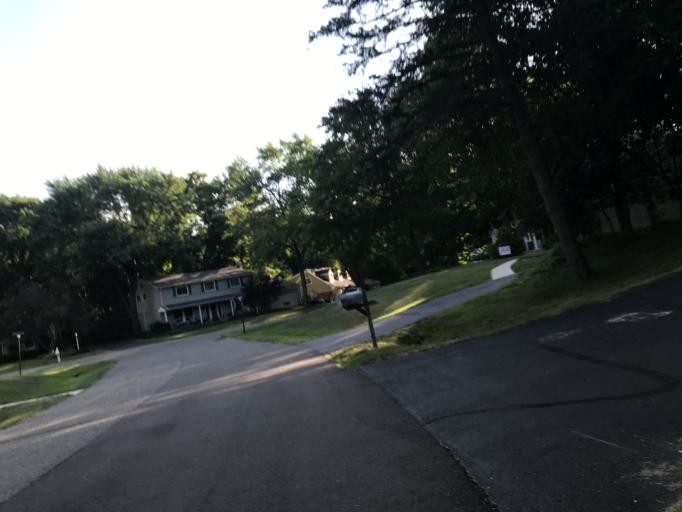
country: US
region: Michigan
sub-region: Oakland County
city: Farmington Hills
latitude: 42.4909
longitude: -83.3463
